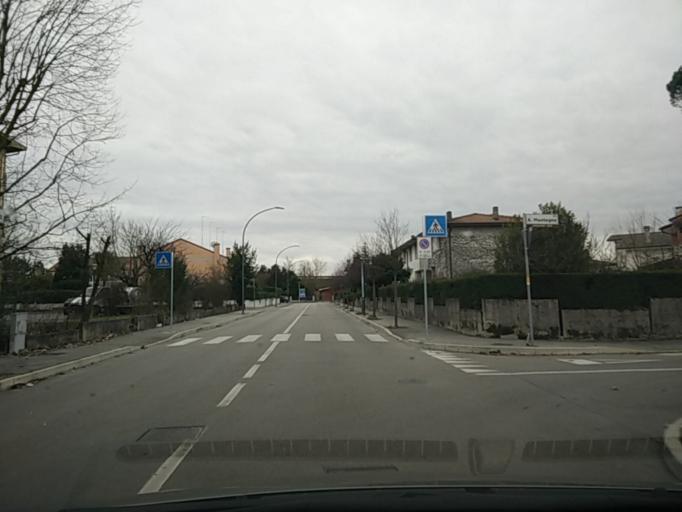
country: IT
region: Veneto
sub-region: Provincia di Treviso
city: Treviso
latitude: 45.6531
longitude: 12.2299
